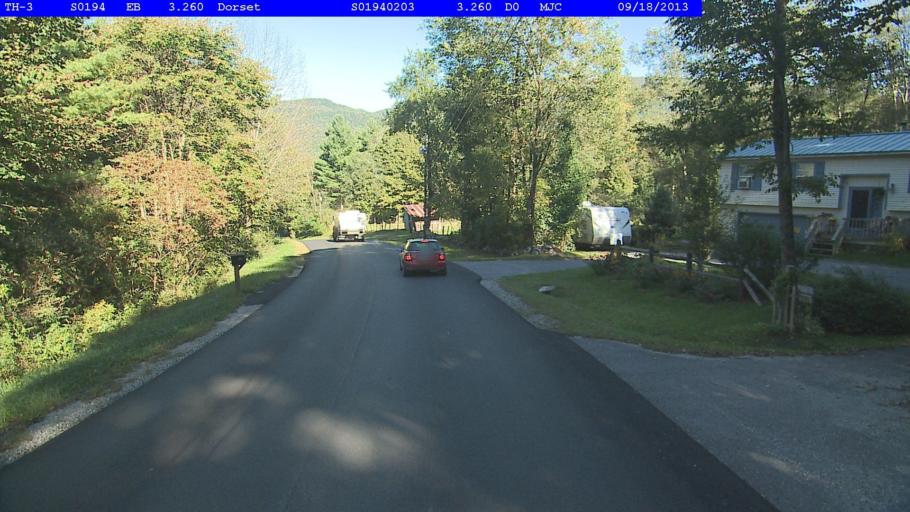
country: US
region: Vermont
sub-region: Bennington County
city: Manchester Center
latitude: 43.2266
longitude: -73.0184
